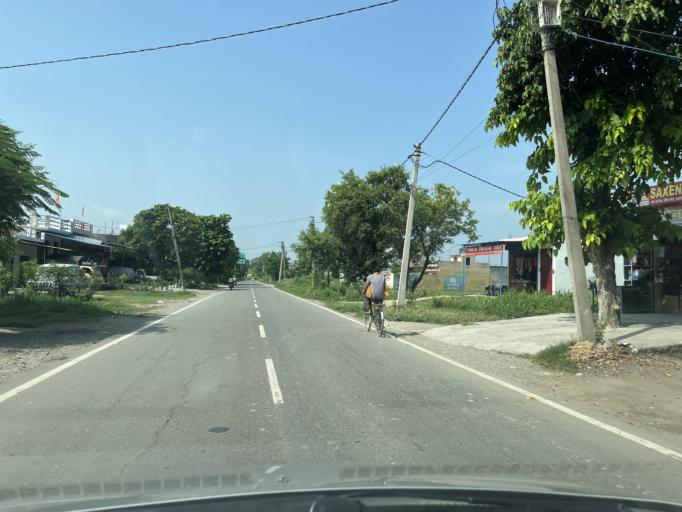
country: IN
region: Uttarakhand
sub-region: Udham Singh Nagar
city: Bazpur
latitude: 29.2041
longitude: 79.2080
